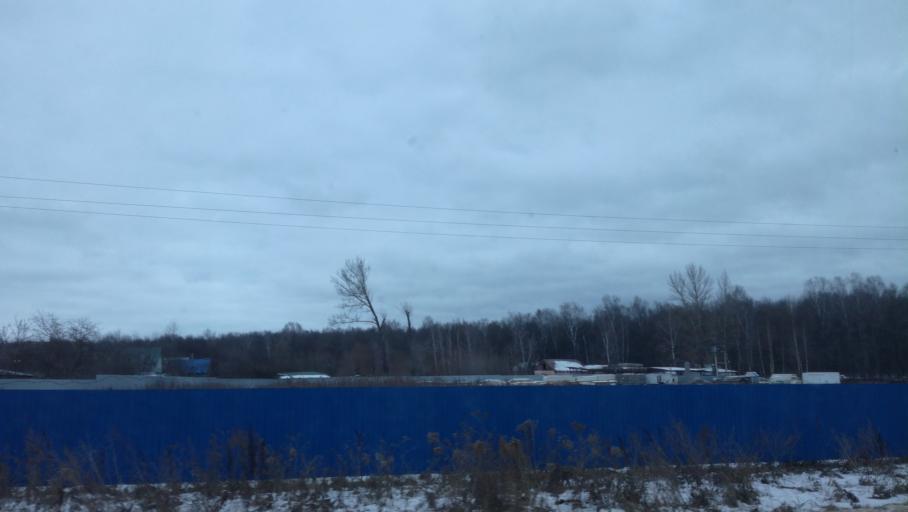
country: RU
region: Tula
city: Kosaya Gora
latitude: 54.1764
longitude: 37.5007
